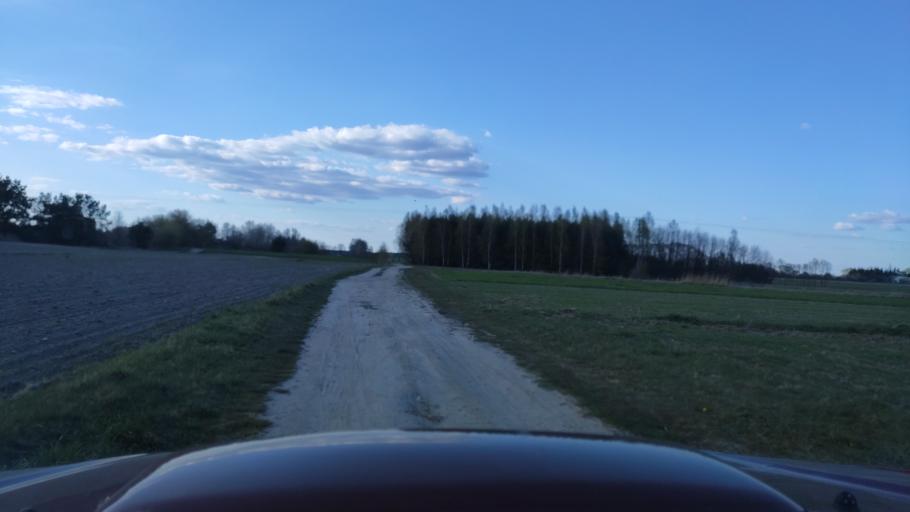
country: PL
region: Masovian Voivodeship
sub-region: Powiat zwolenski
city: Zwolen
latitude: 51.3669
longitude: 21.5752
